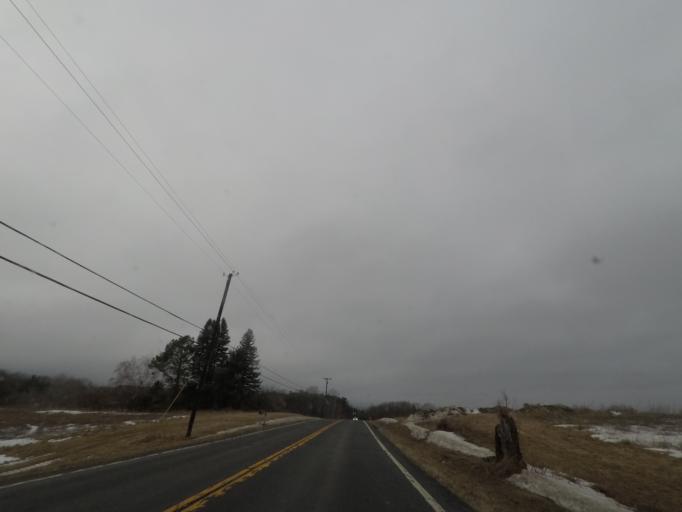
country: US
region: New York
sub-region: Albany County
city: Voorheesville
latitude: 42.6566
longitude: -73.9776
